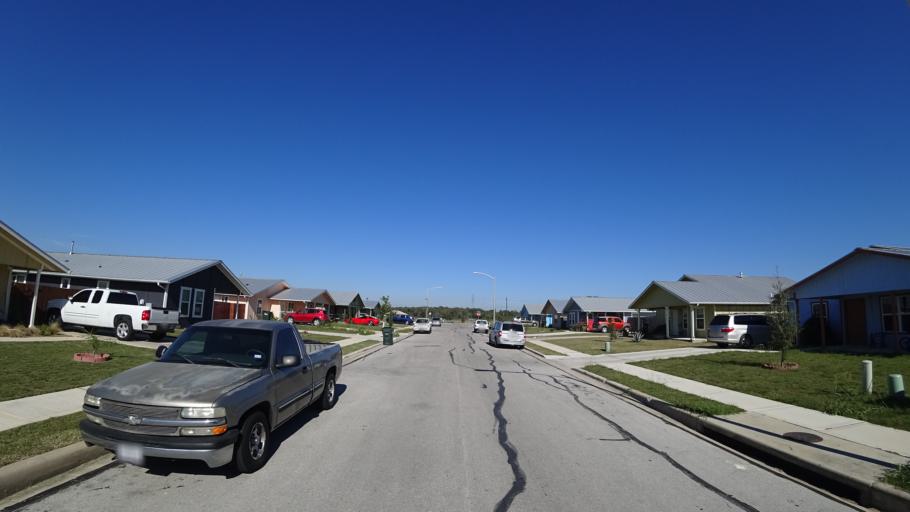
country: US
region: Texas
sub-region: Travis County
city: Hornsby Bend
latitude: 30.2578
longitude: -97.5904
